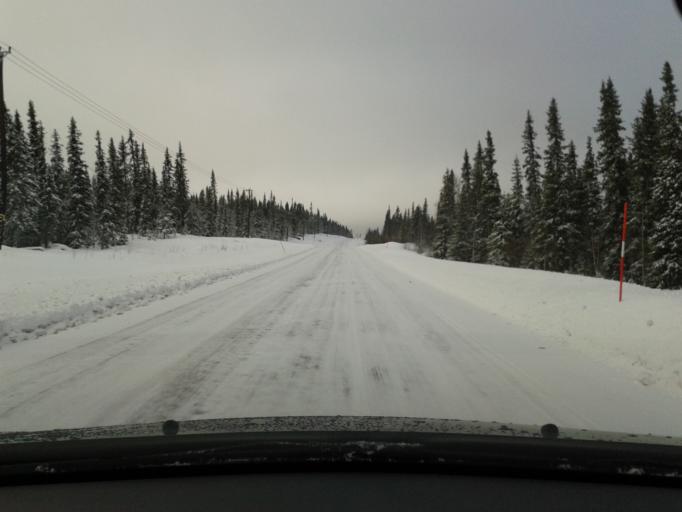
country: SE
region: Vaesterbotten
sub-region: Vilhelmina Kommun
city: Sjoberg
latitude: 65.2090
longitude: 16.0108
